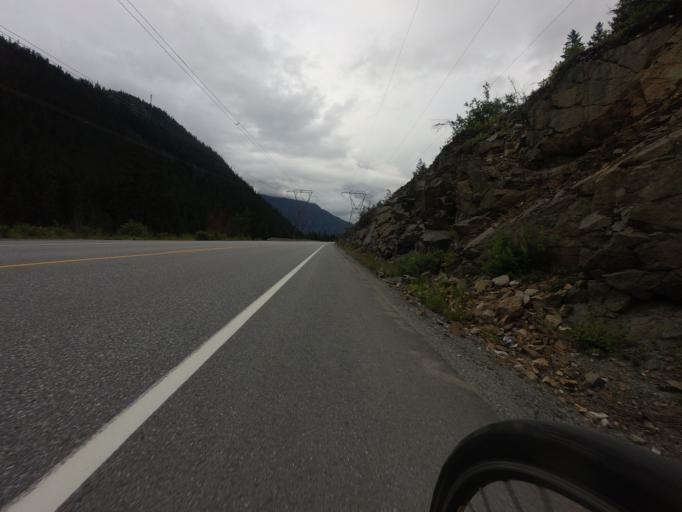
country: CA
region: British Columbia
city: Pemberton
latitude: 50.2353
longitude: -122.8695
